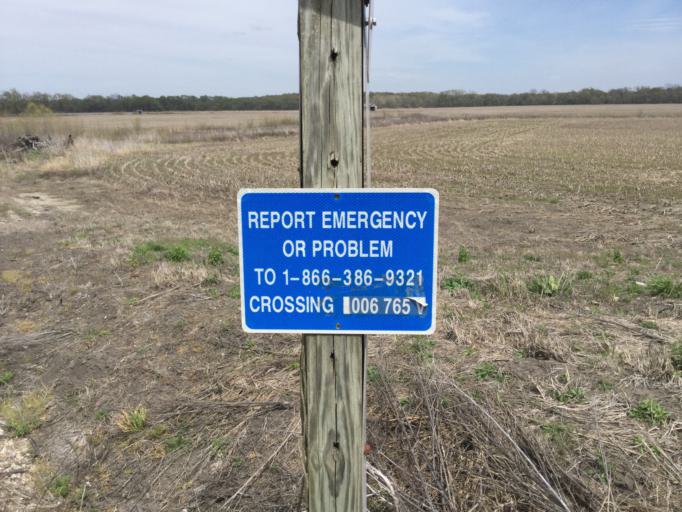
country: US
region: Kansas
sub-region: Neosho County
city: Chanute
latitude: 37.7180
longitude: -95.4391
